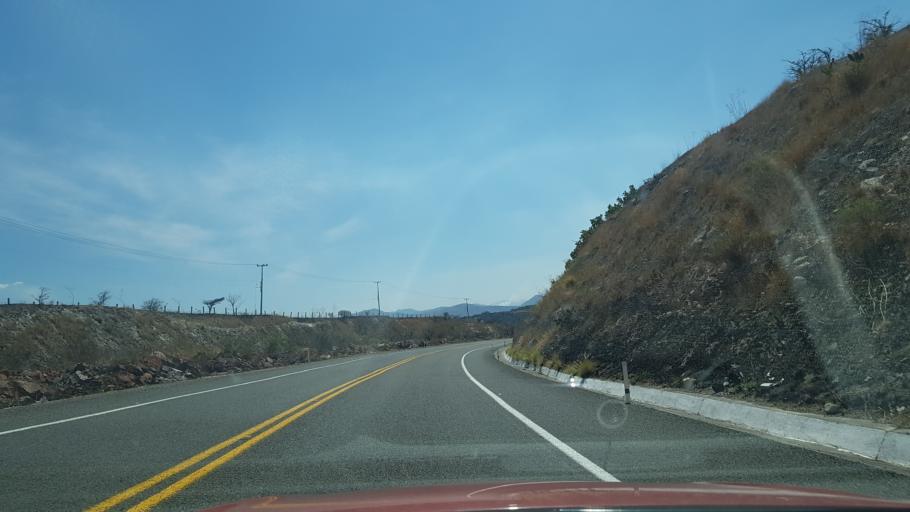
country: MX
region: Michoacan
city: Alvaro Obregon
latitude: 19.7963
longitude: -101.0203
